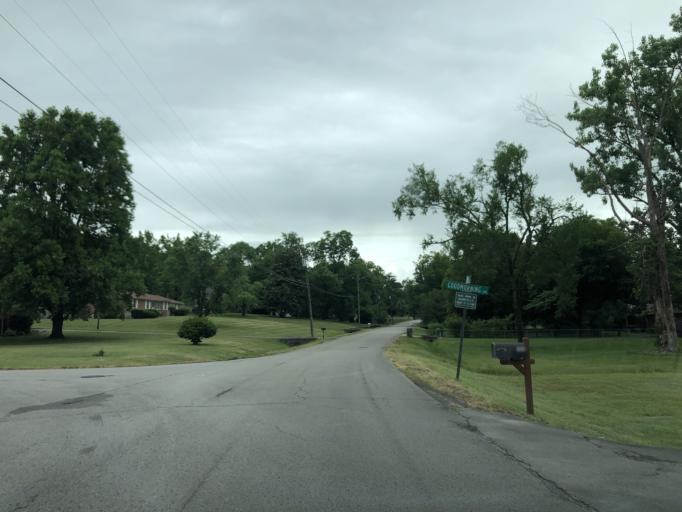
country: US
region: Tennessee
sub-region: Davidson County
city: Goodlettsville
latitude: 36.2729
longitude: -86.7658
